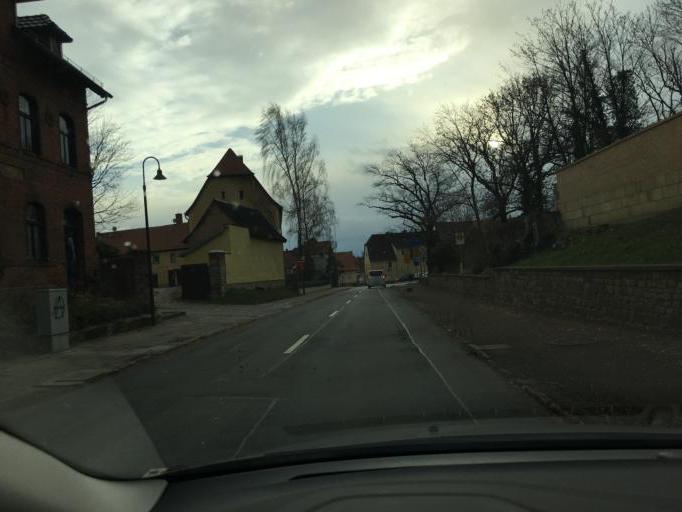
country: DE
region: Saxony-Anhalt
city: Bad Lauchstadt
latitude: 51.3889
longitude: 11.8695
